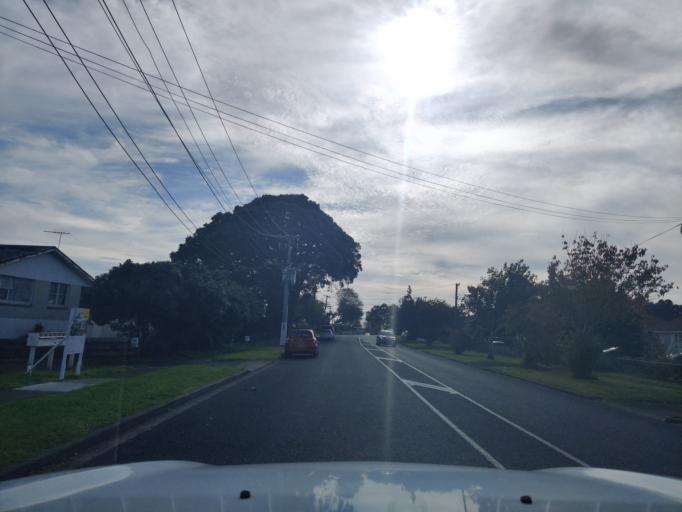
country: NZ
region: Auckland
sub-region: Auckland
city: Tamaki
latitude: -36.8972
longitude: 174.8547
